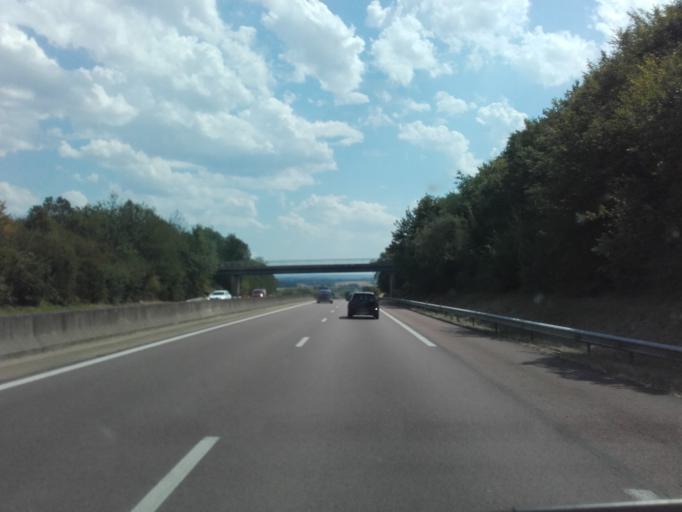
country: FR
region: Bourgogne
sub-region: Departement de l'Yonne
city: Avallon
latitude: 47.5216
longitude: 3.9880
